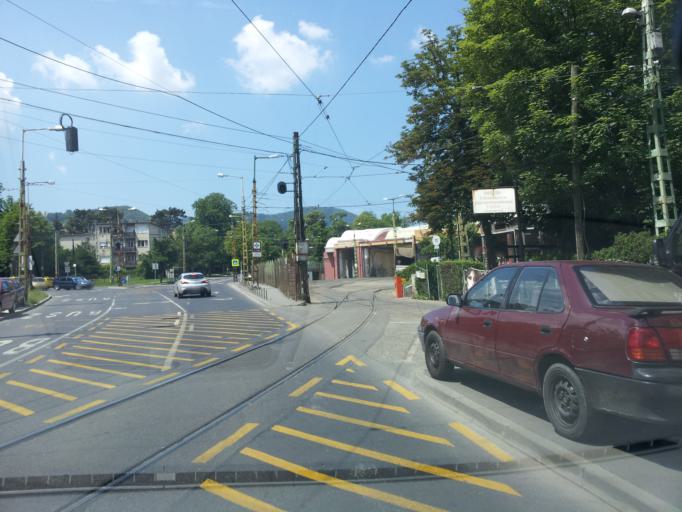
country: HU
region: Budapest
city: Budapest XII. keruelet
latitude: 47.5177
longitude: 18.9944
